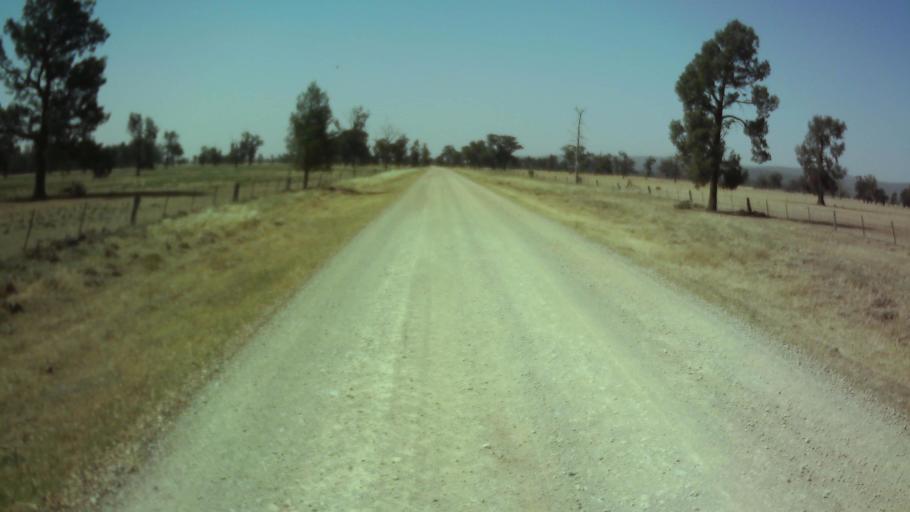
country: AU
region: New South Wales
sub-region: Weddin
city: Grenfell
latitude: -34.0255
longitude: 147.9136
